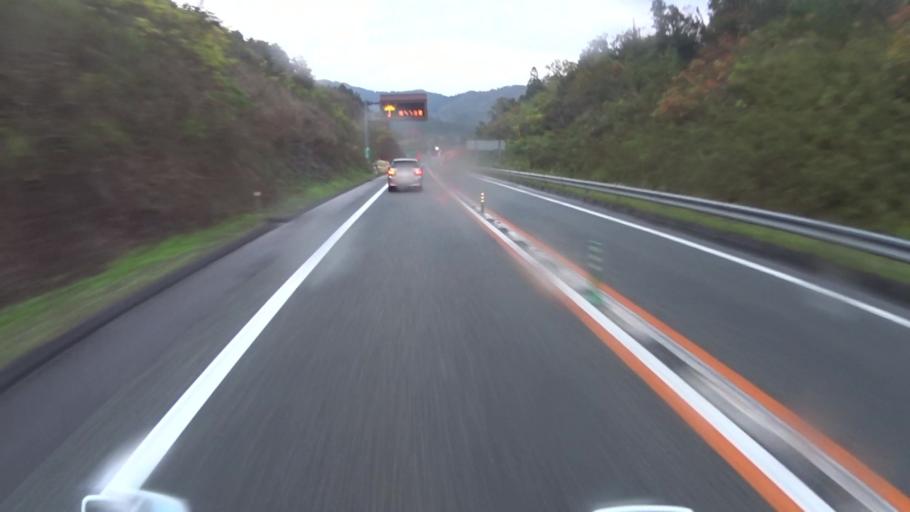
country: JP
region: Kyoto
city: Ayabe
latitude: 35.3412
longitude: 135.3039
